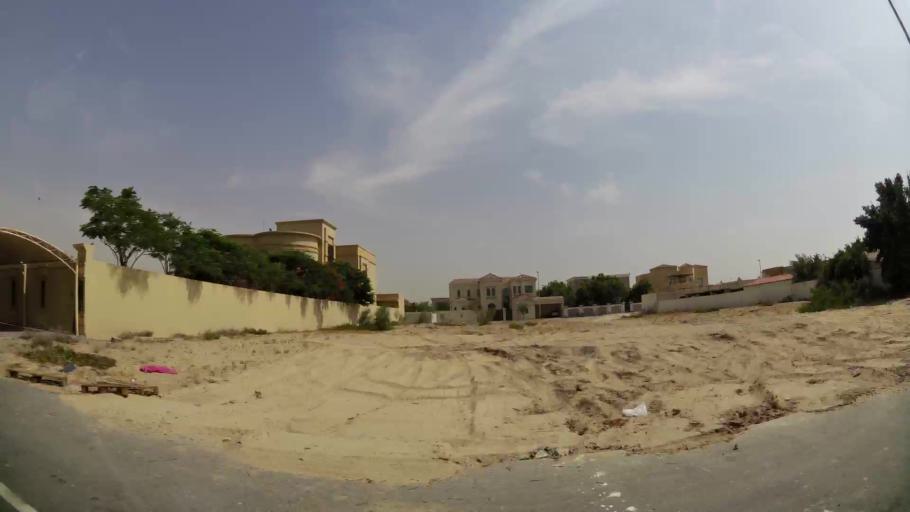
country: AE
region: Ash Shariqah
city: Sharjah
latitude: 25.2353
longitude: 55.4495
